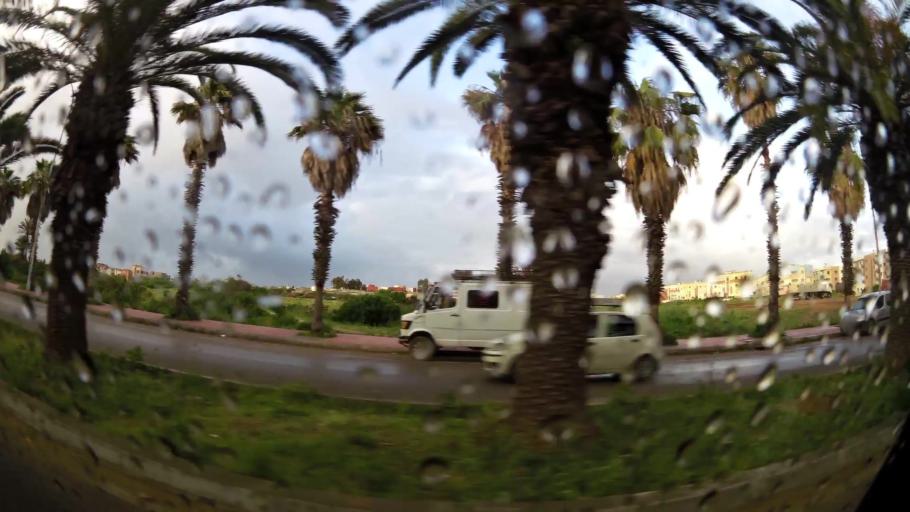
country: MA
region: Doukkala-Abda
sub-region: El-Jadida
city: El Jadida
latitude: 33.2306
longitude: -8.4892
